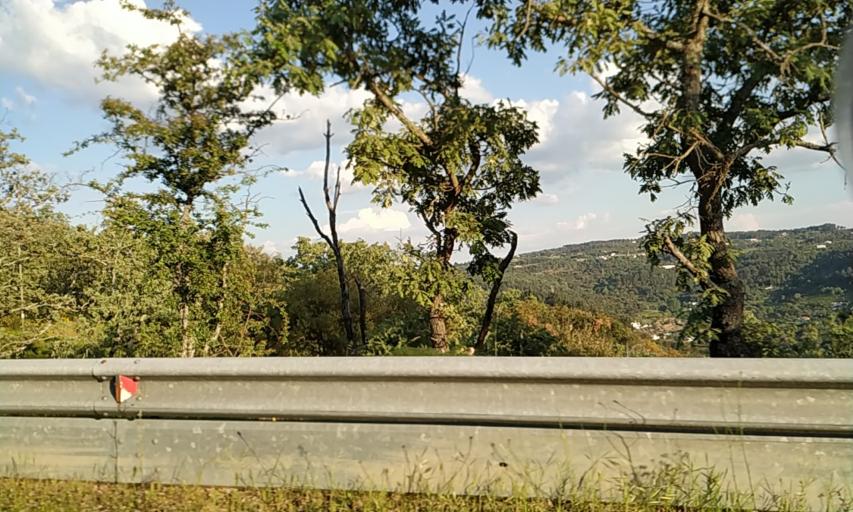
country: PT
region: Portalegre
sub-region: Portalegre
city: Portalegre
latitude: 39.3330
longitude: -7.4263
